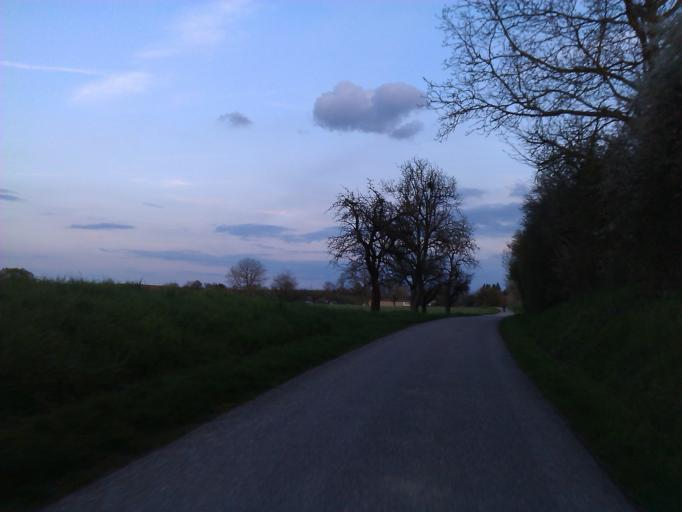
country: DE
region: Baden-Wuerttemberg
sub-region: Regierungsbezirk Stuttgart
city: Bad Wimpfen
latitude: 49.2247
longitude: 9.1688
